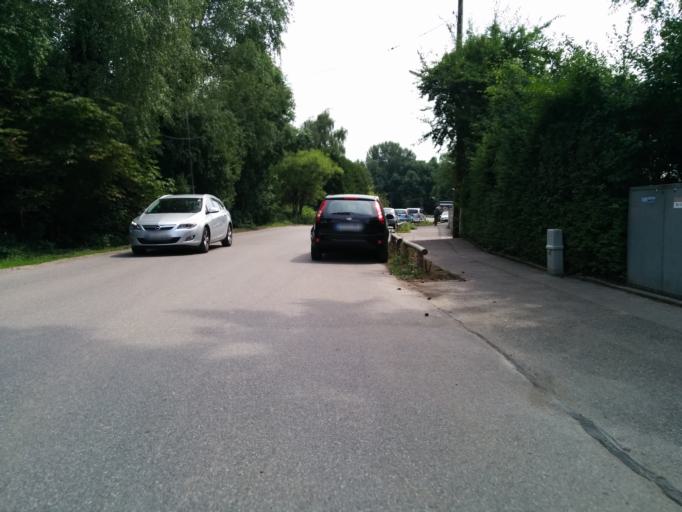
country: DE
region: Bavaria
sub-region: Upper Bavaria
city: Karlsfeld
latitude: 48.2012
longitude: 11.4553
